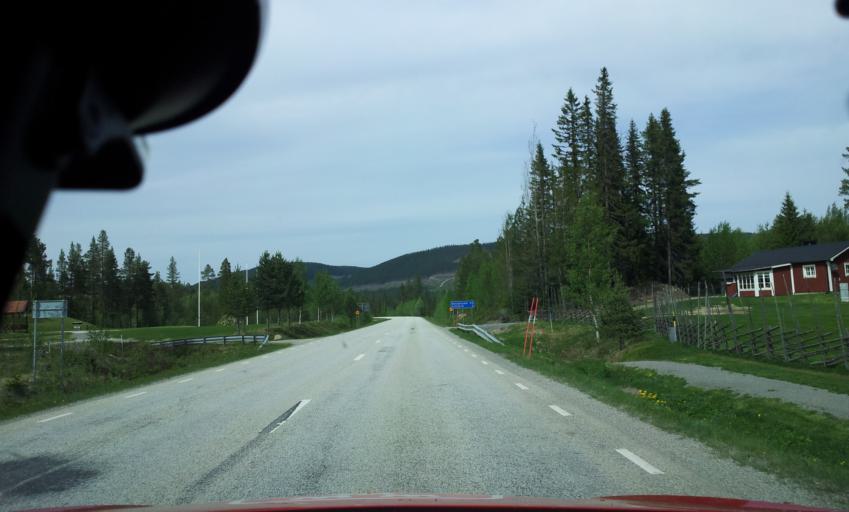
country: SE
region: Jaemtland
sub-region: Bergs Kommun
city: Hoverberg
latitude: 62.4795
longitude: 14.2298
